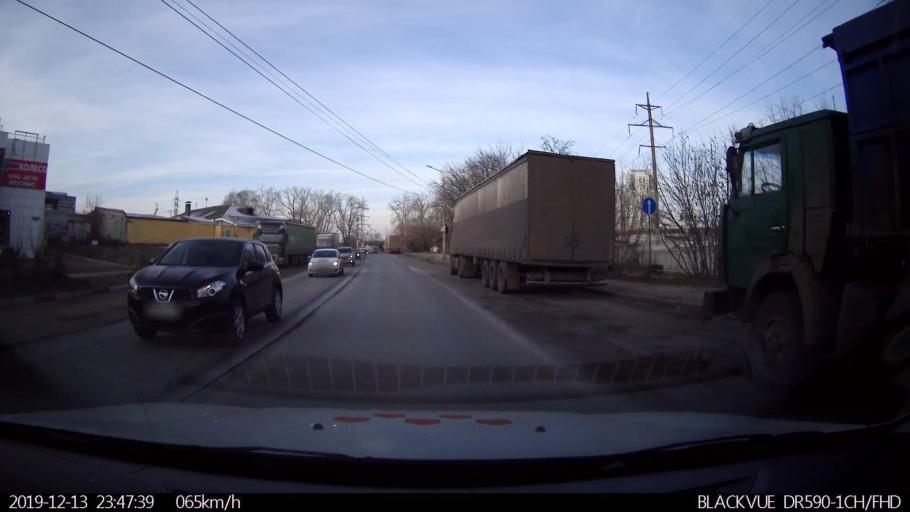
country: RU
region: Nizjnij Novgorod
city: Nizhniy Novgorod
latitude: 56.2959
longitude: 43.9519
